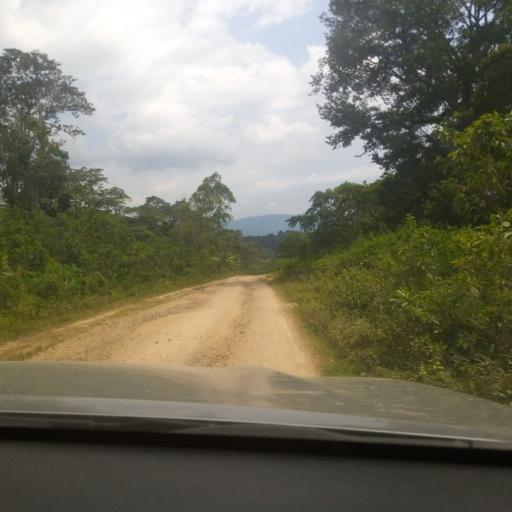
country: ET
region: Southern Nations, Nationalities, and People's Region
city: Tippi
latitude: 7.1325
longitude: 35.4263
